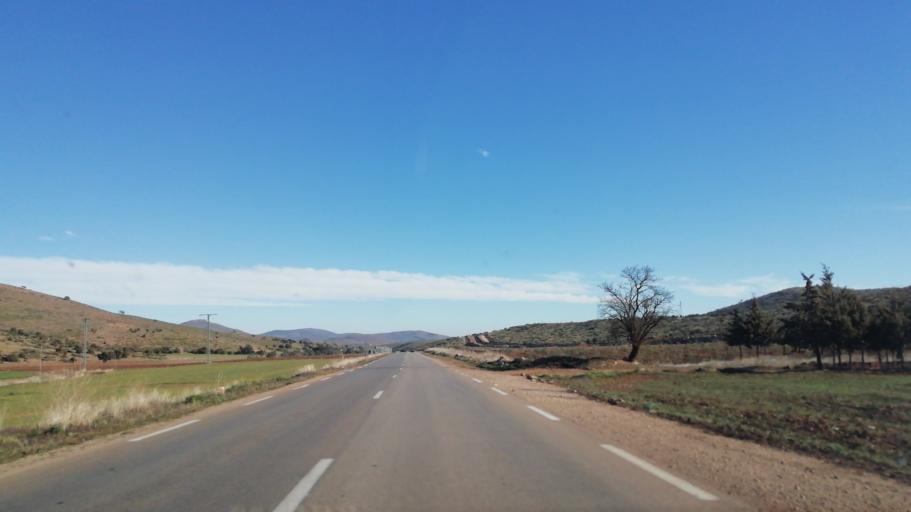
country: DZ
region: Tlemcen
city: Tlemcen
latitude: 34.7468
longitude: -1.1625
